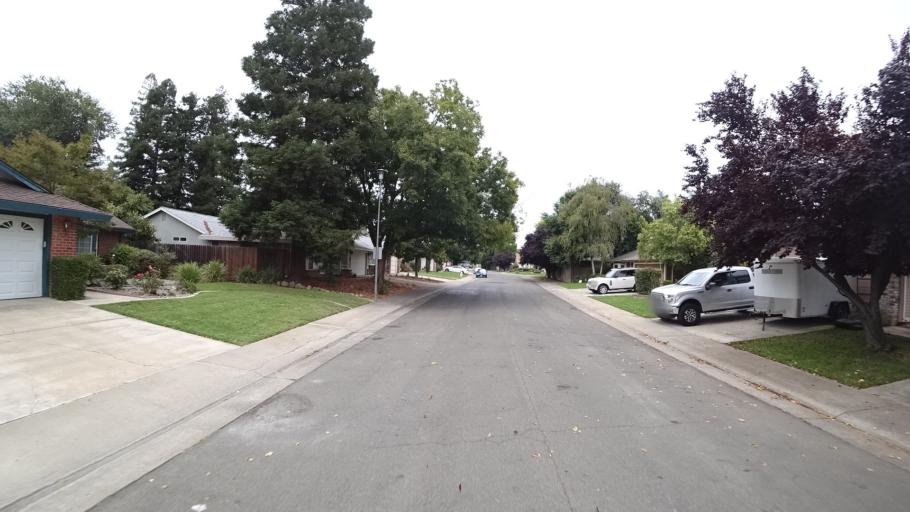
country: US
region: California
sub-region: Sacramento County
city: Laguna
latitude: 38.4214
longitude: -121.4346
